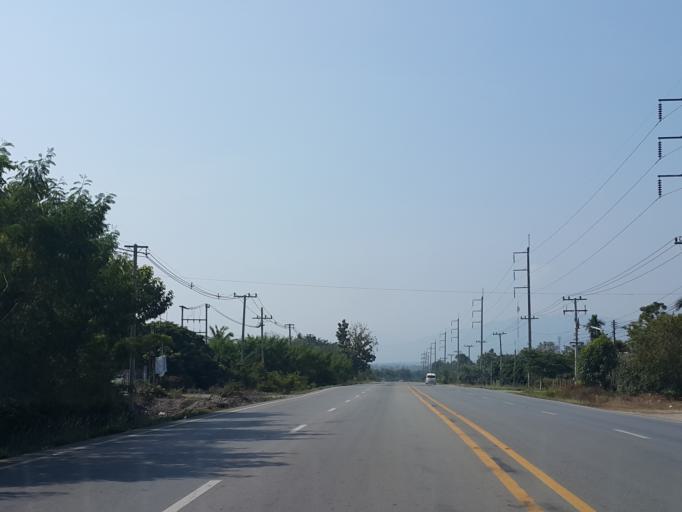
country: TH
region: Chiang Mai
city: Chom Thong
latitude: 18.3145
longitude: 98.6594
